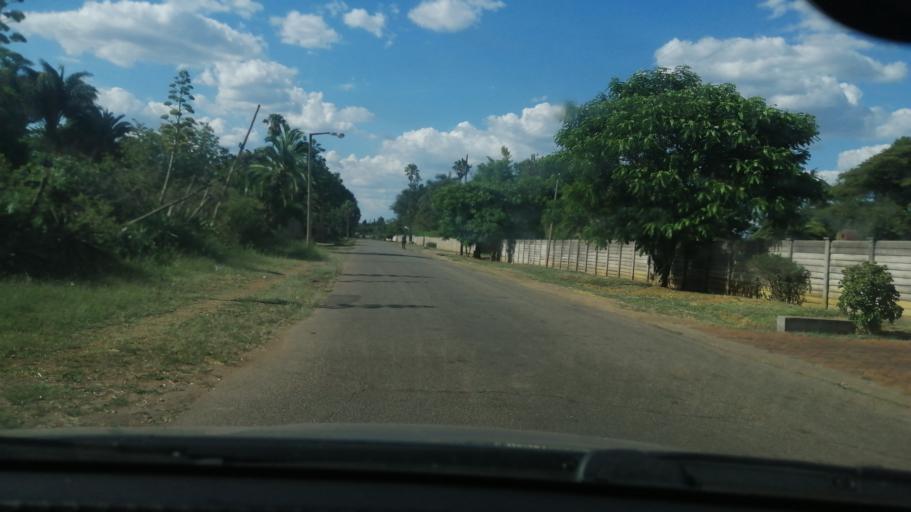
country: ZW
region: Harare
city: Harare
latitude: -17.7744
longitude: 31.0637
